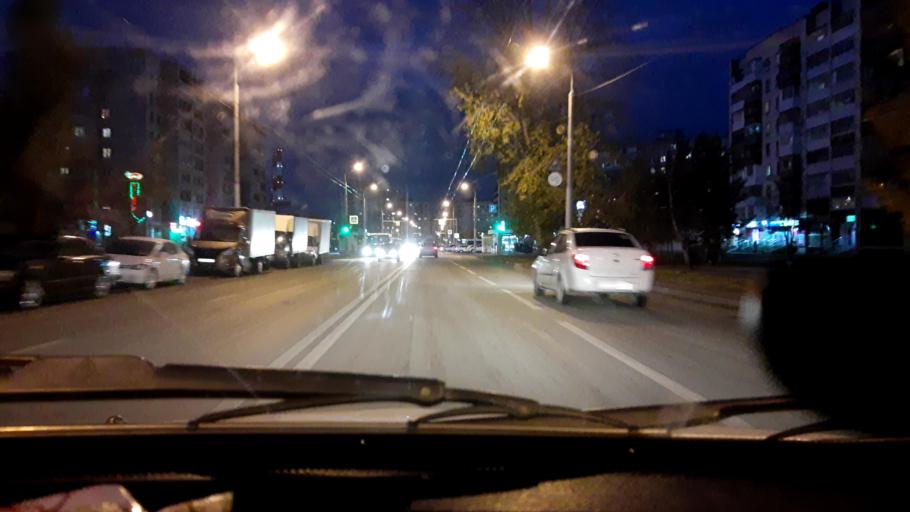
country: RU
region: Bashkortostan
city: Ufa
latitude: 54.7769
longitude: 56.1145
